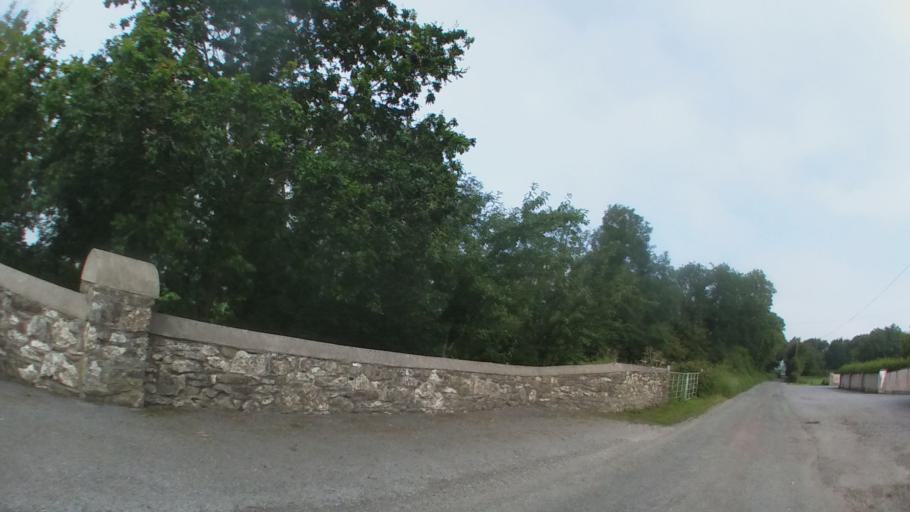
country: IE
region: Leinster
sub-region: Kilkenny
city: Kilkenny
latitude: 52.6900
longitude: -7.1883
